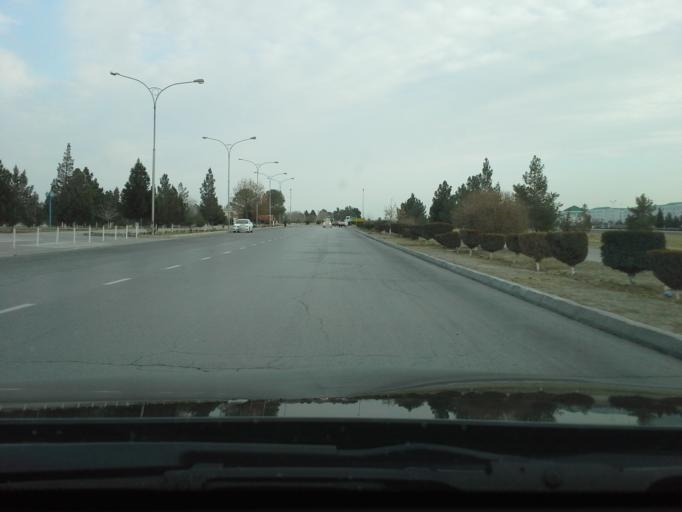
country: TM
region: Ahal
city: Ashgabat
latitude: 37.9888
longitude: 58.3264
